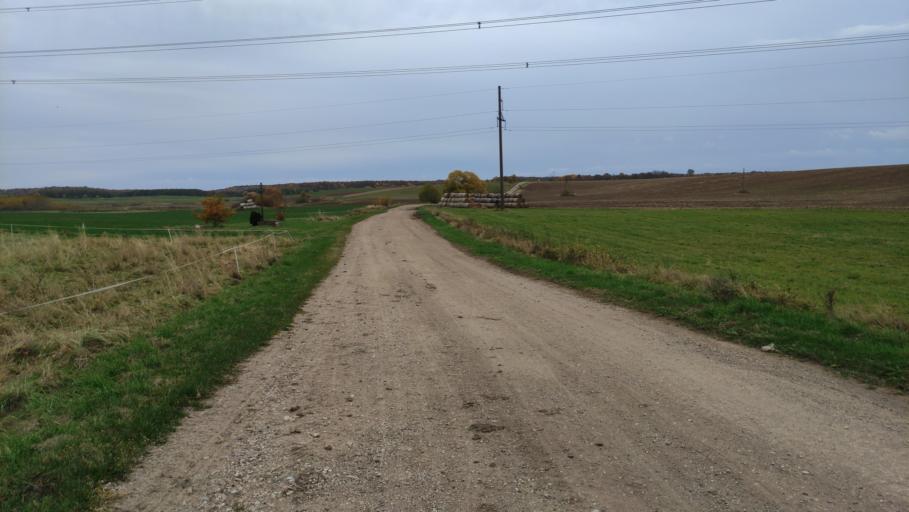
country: LT
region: Alytaus apskritis
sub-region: Alytus
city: Alytus
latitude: 54.4221
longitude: 23.8646
